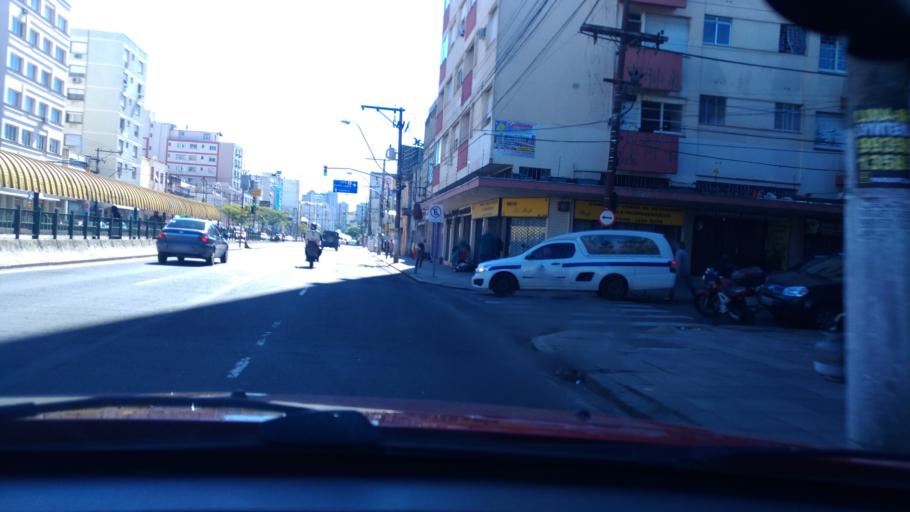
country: BR
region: Rio Grande do Sul
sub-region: Porto Alegre
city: Porto Alegre
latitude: -30.0422
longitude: -51.2154
